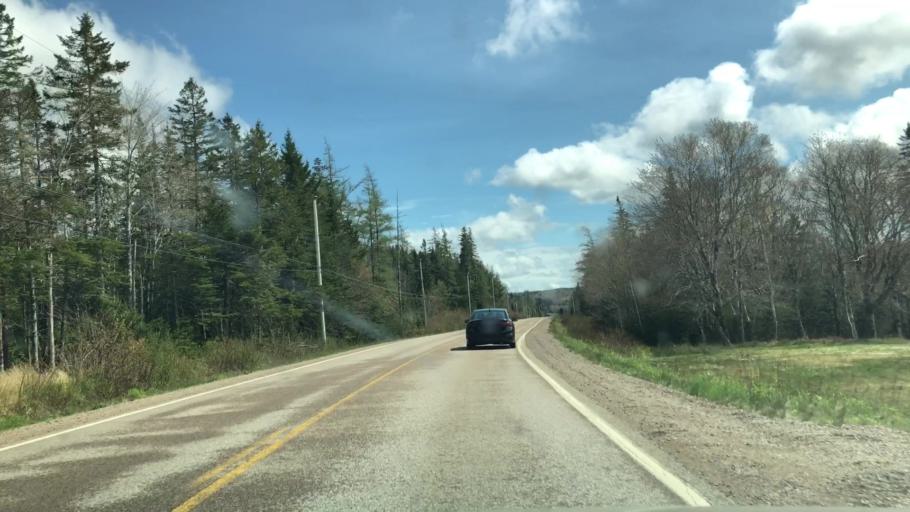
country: CA
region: Nova Scotia
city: Antigonish
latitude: 45.2095
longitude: -62.0039
